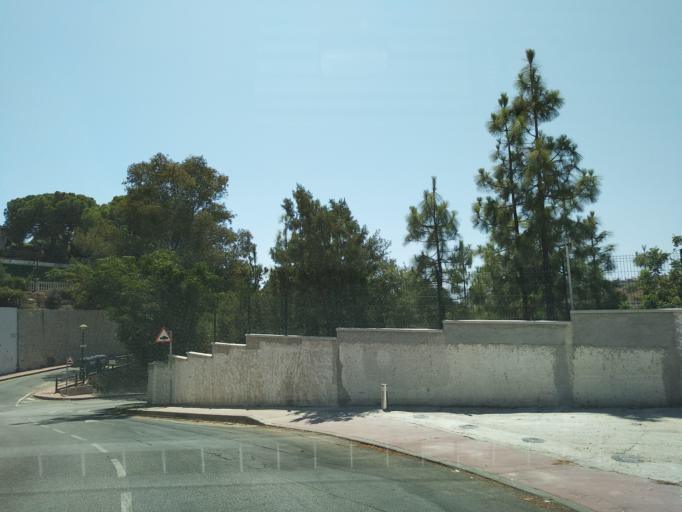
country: ES
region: Andalusia
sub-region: Provincia de Malaga
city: Malaga
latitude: 36.7294
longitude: -4.3816
